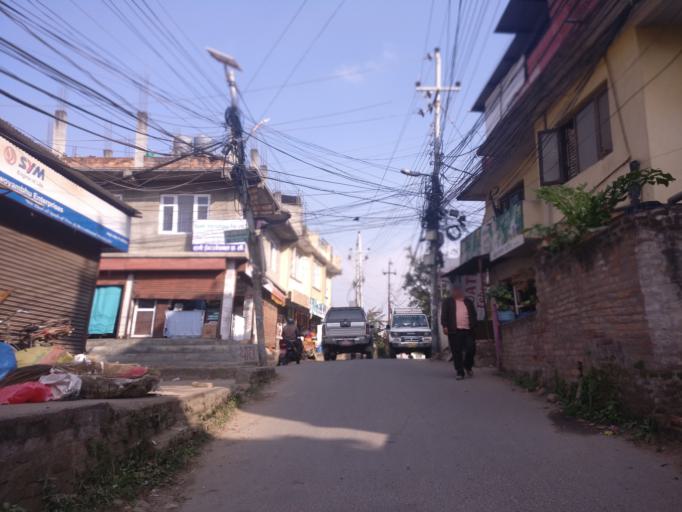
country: NP
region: Central Region
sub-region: Bagmati Zone
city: Patan
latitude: 27.6853
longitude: 85.3205
